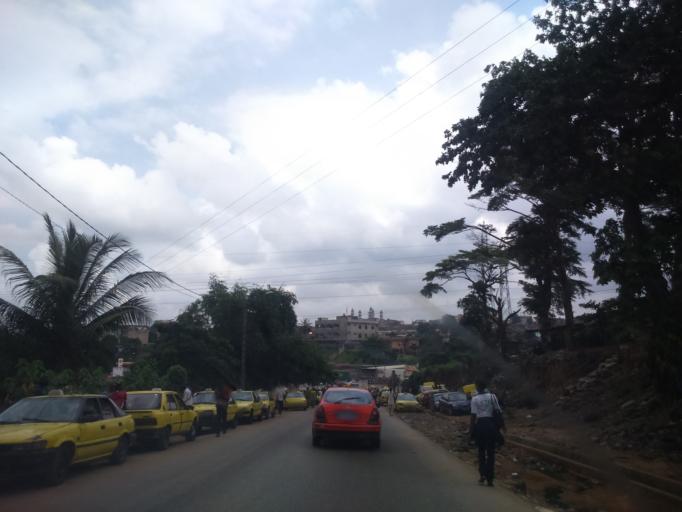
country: CI
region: Lagunes
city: Abobo
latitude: 5.3651
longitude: -4.0145
